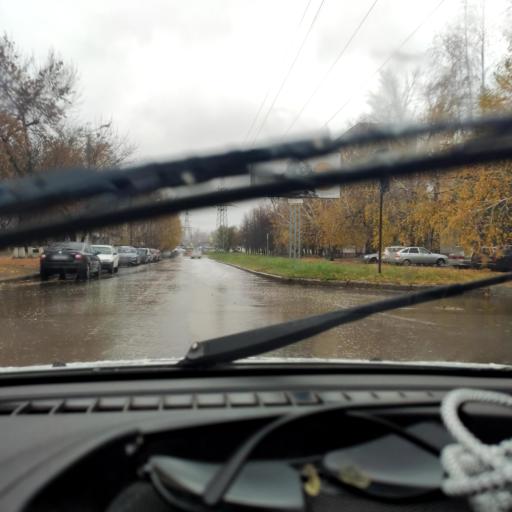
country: RU
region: Samara
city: Tol'yatti
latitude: 53.5130
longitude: 49.4421
